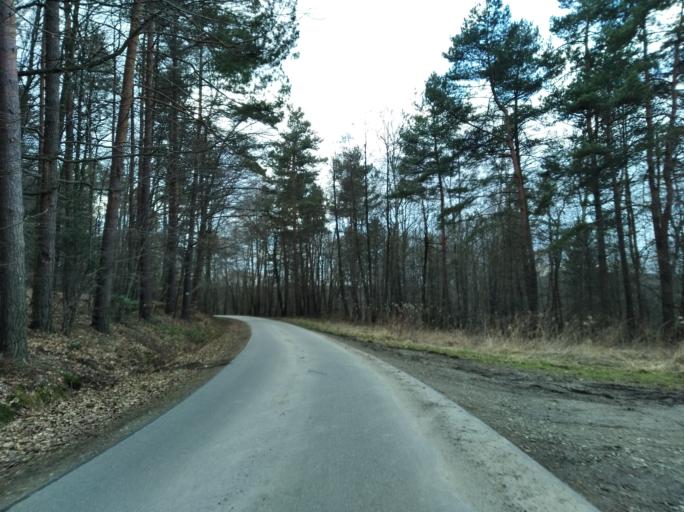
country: PL
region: Subcarpathian Voivodeship
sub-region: Powiat strzyzowski
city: Wysoka Strzyzowska
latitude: 49.7978
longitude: 21.7286
